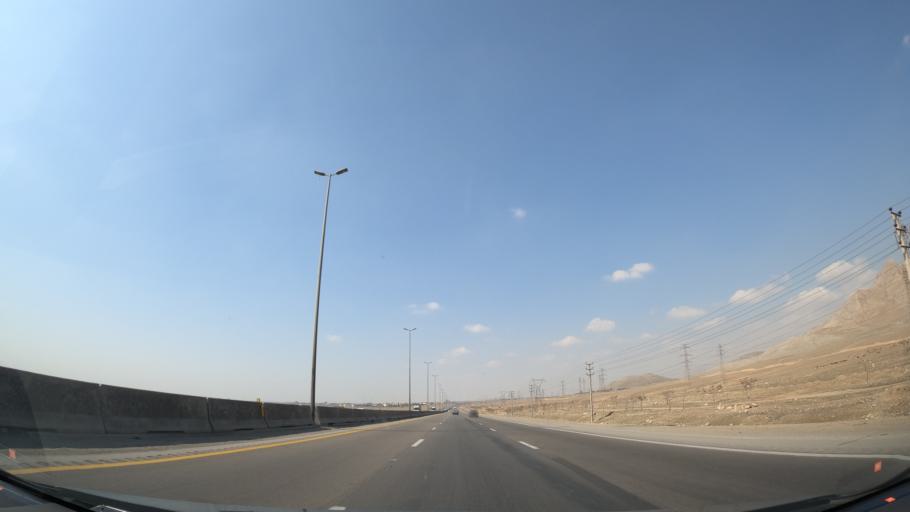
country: IR
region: Qazvin
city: Abyek
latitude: 36.0554
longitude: 50.5084
